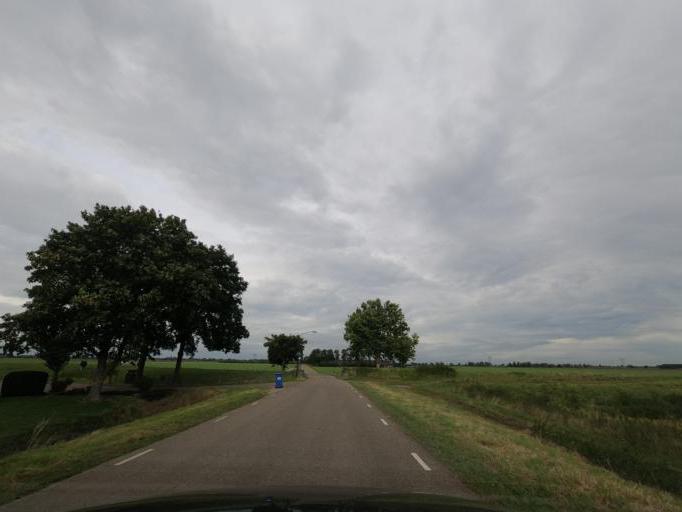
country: NL
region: North Brabant
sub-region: Gemeente Waalwijk
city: Waspik
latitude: 51.6963
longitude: 4.9246
